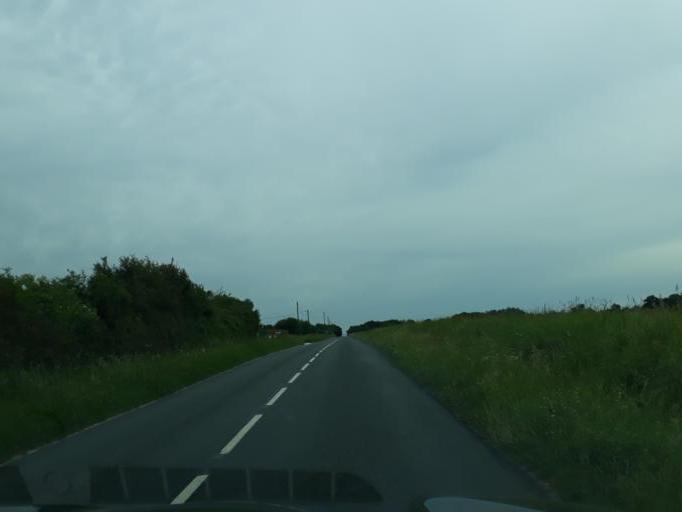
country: FR
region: Centre
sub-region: Departement du Loiret
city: Saint-Pere-sur-Loire
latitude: 47.7389
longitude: 2.3516
